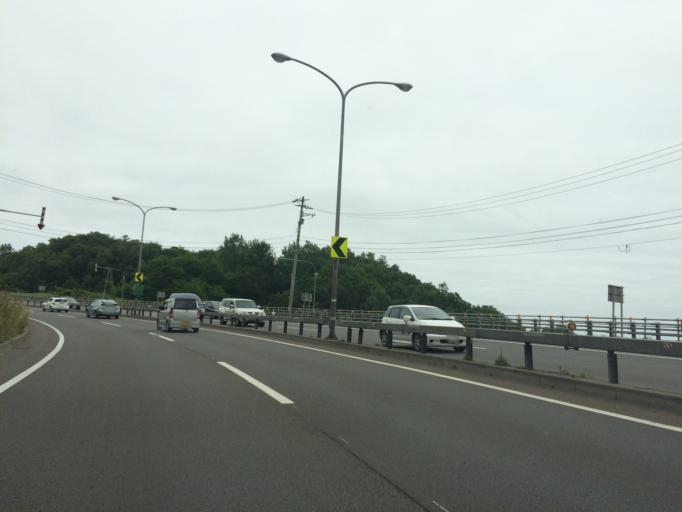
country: JP
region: Hokkaido
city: Otaru
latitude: 43.1560
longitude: 141.1117
